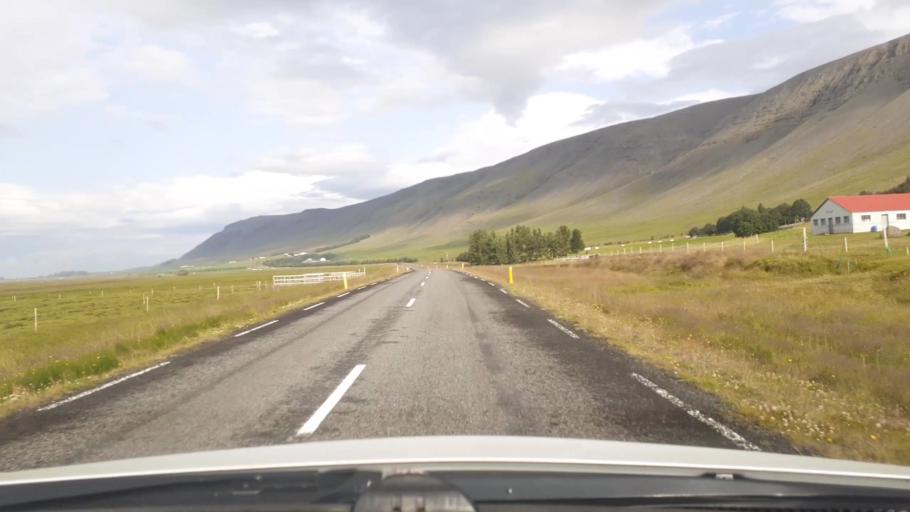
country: IS
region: Capital Region
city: Mosfellsbaer
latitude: 64.3331
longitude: -21.5203
